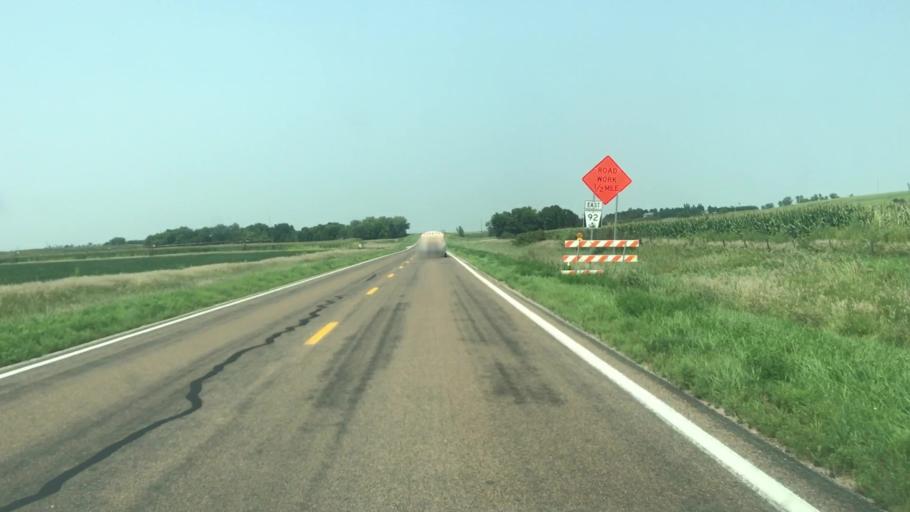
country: US
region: Nebraska
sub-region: Sherman County
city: Loup City
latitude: 41.2554
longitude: -98.9389
